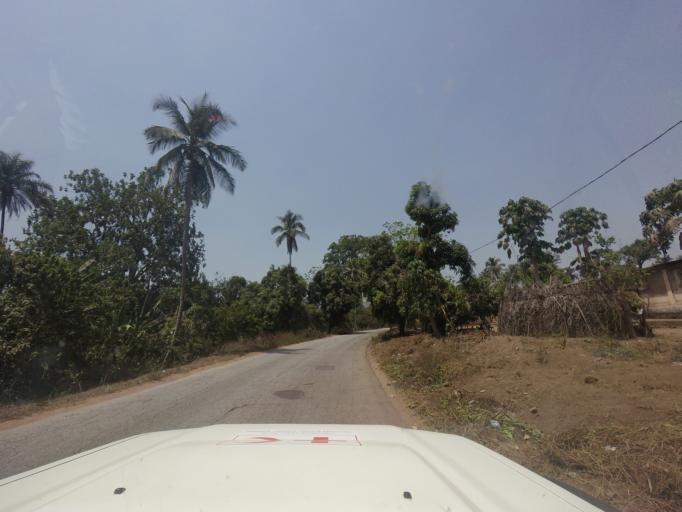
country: GN
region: Kindia
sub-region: Coyah
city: Coyah
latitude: 9.8332
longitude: -13.1070
